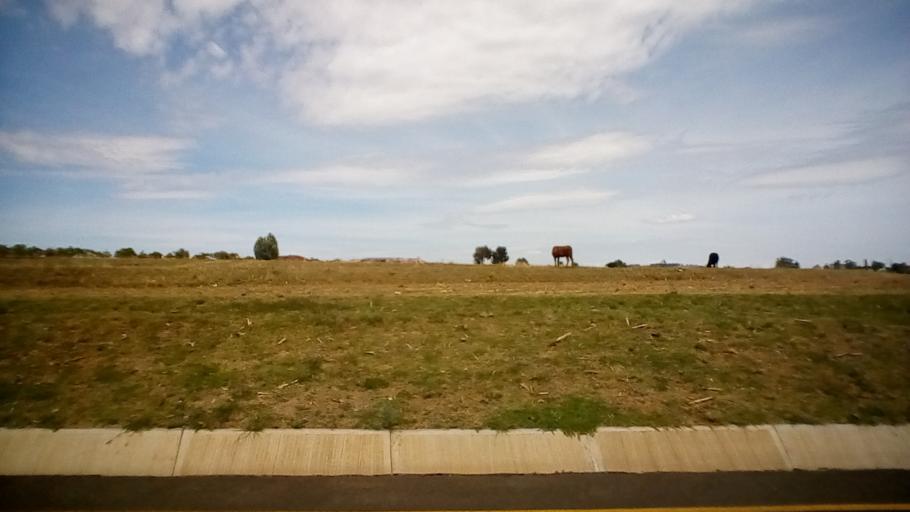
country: LS
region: Leribe
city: Maputsoe
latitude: -28.9447
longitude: 27.9363
